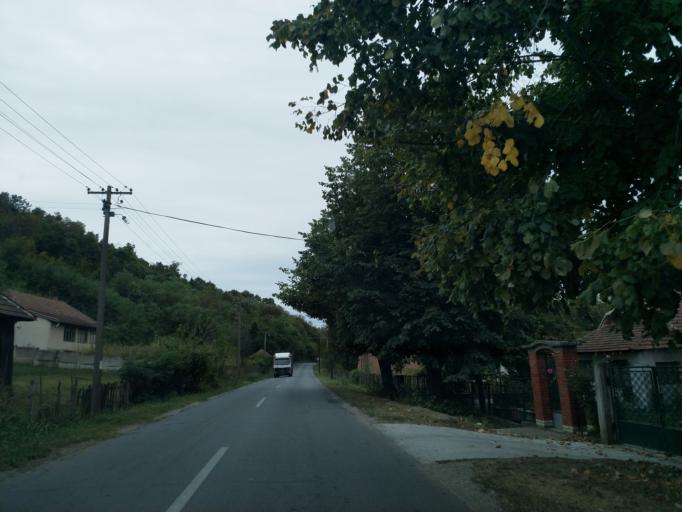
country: RS
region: Central Serbia
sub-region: Pomoravski Okrug
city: Jagodina
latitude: 44.0616
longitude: 21.1820
